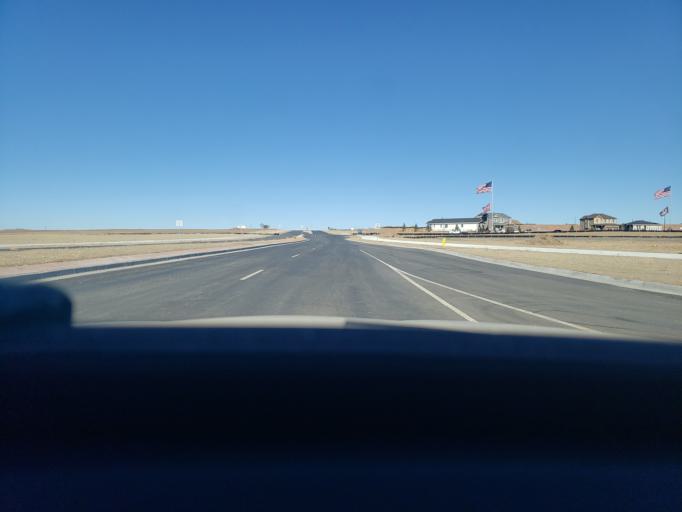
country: US
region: Colorado
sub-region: Adams County
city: Aurora
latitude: 39.7712
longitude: -104.7065
